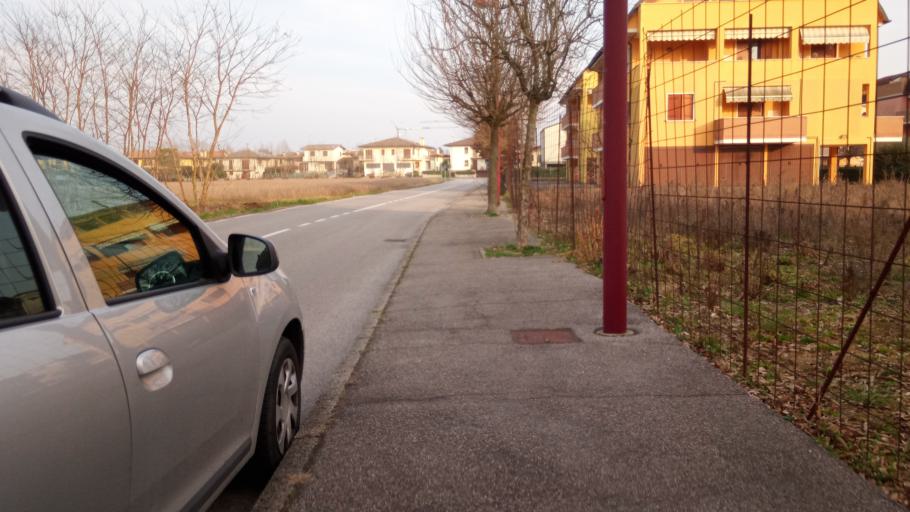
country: IT
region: Veneto
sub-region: Provincia di Padova
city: Rubano
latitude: 45.4313
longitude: 11.7859
